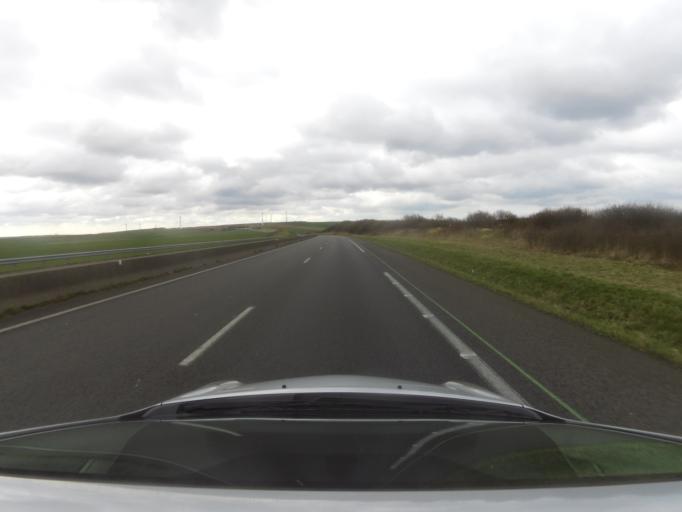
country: FR
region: Nord-Pas-de-Calais
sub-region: Departement du Pas-de-Calais
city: Dannes
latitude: 50.5910
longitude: 1.6421
